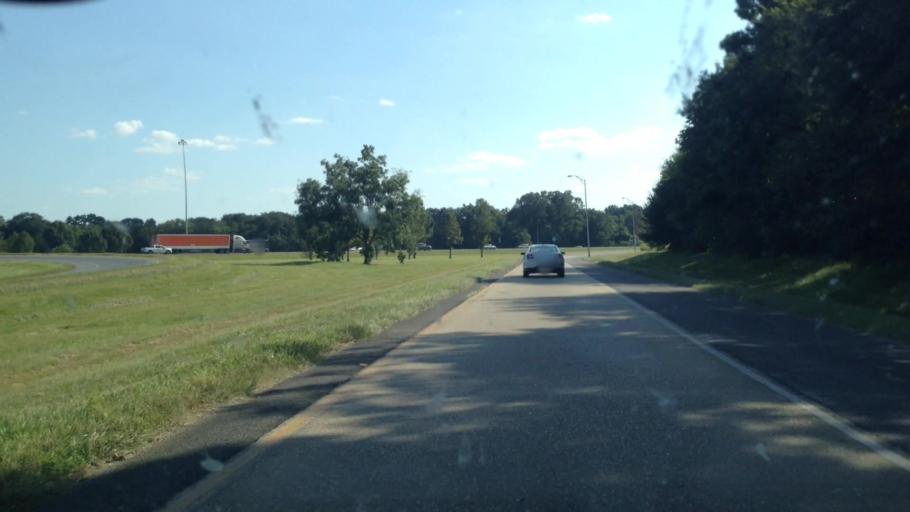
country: US
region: Louisiana
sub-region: Lafayette Parish
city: Lafayette
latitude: 30.2606
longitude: -92.0179
